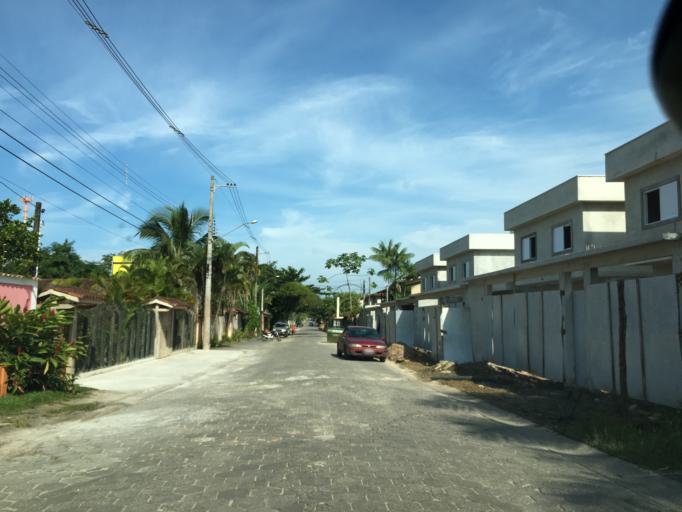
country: BR
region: Sao Paulo
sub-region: Sao Sebastiao
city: Sao Sebastiao
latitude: -23.7591
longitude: -45.7264
